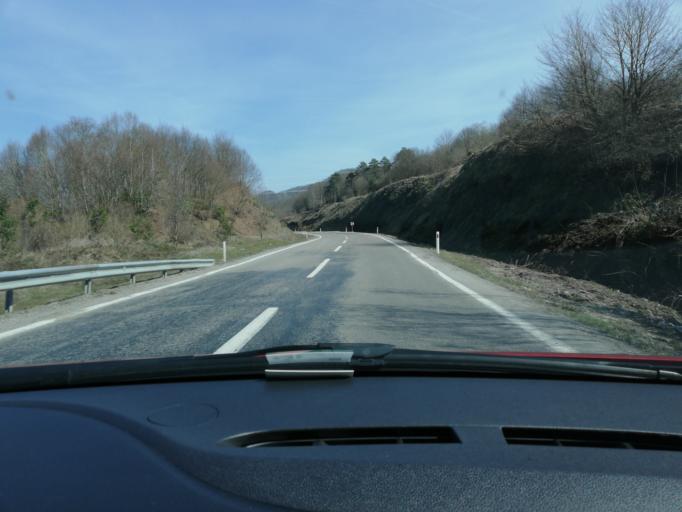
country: TR
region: Bartin
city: Amasra
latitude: 41.7052
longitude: 32.3895
